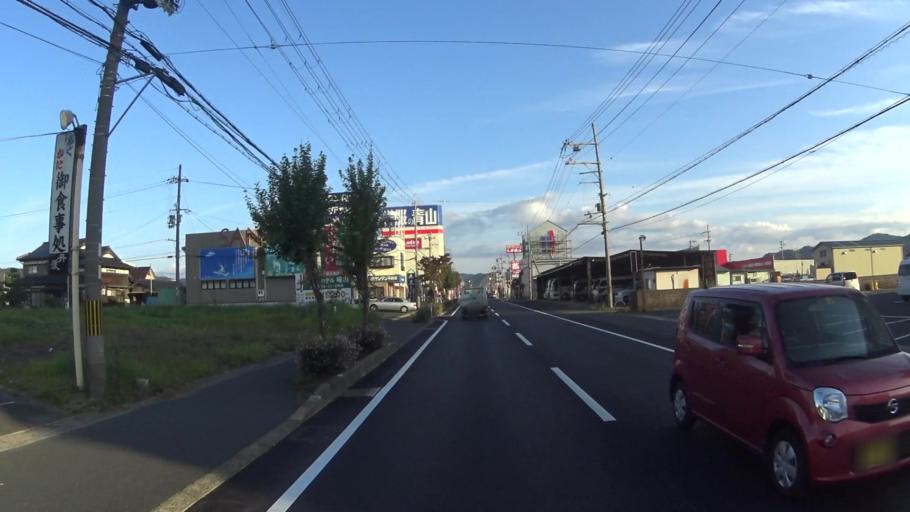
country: JP
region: Kyoto
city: Miyazu
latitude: 35.6060
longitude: 135.0824
